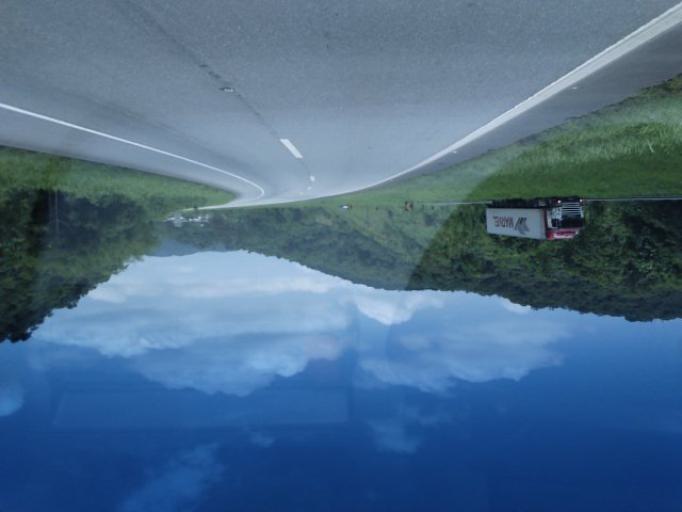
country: BR
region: Sao Paulo
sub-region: Miracatu
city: Miracatu
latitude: -24.1940
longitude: -47.3610
